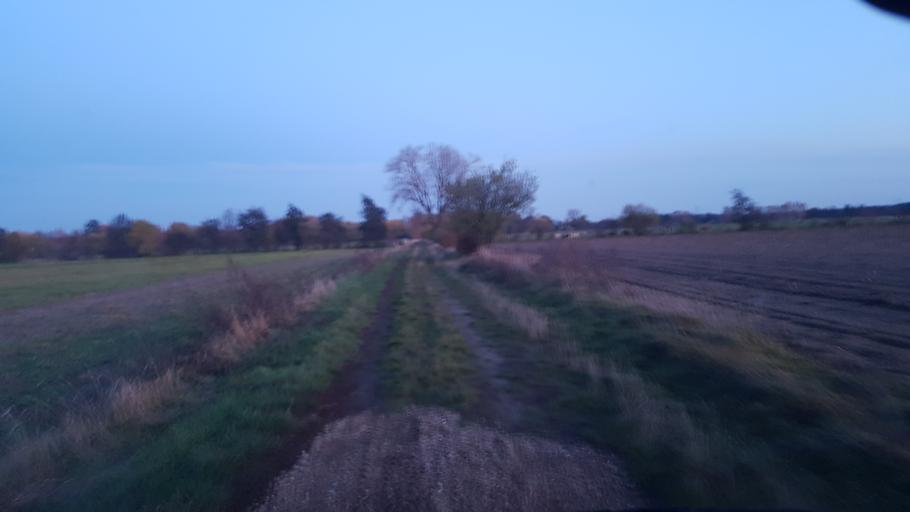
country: DE
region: Brandenburg
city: Schilda
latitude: 51.6205
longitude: 13.3465
